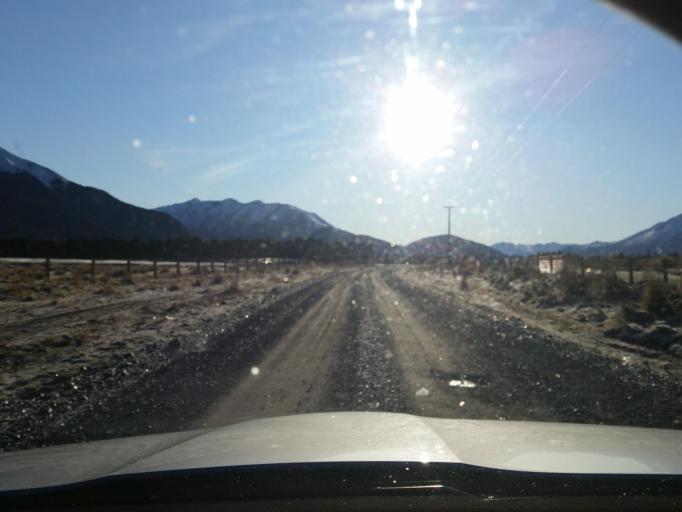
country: NZ
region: Southland
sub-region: Southland District
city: Te Anau
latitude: -45.3521
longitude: 168.1379
